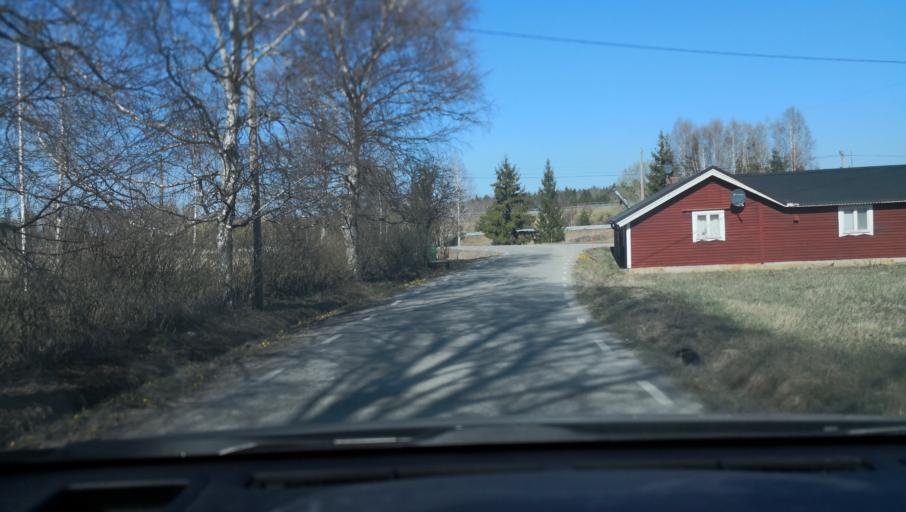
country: SE
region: Vaestmanland
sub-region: Sala Kommun
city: Sala
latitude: 59.9065
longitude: 16.5311
